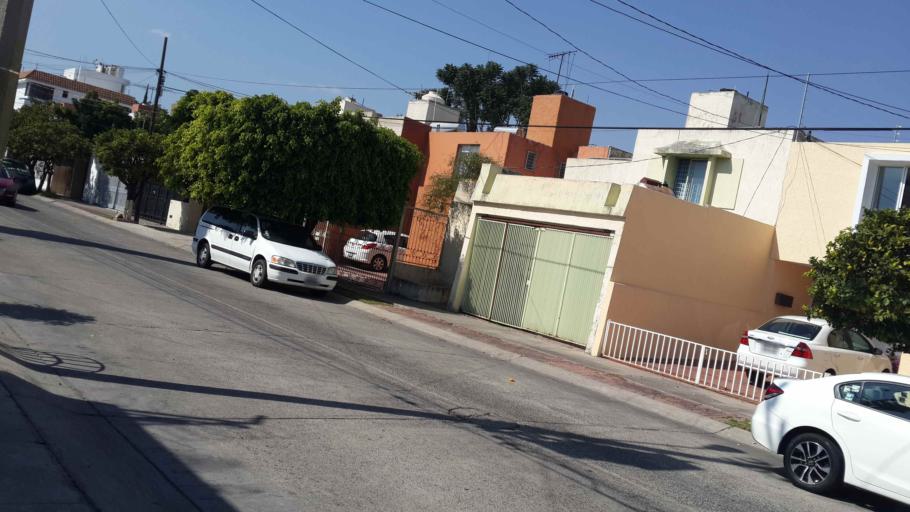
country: MX
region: Jalisco
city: Guadalajara
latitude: 20.6680
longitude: -103.4304
